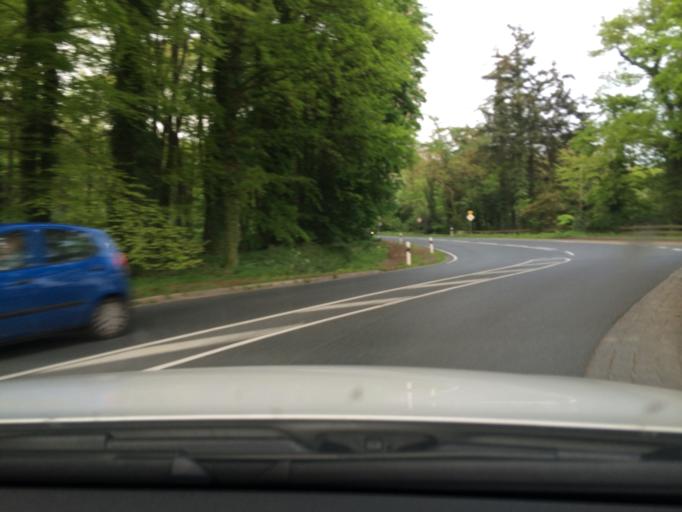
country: DE
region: Lower Saxony
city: Ganderkesee
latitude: 53.0306
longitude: 8.5796
